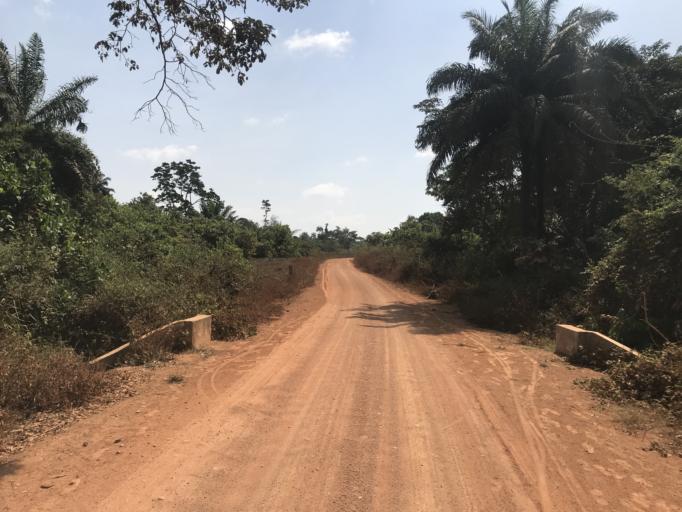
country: NG
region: Osun
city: Ifon
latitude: 7.9060
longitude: 4.4791
